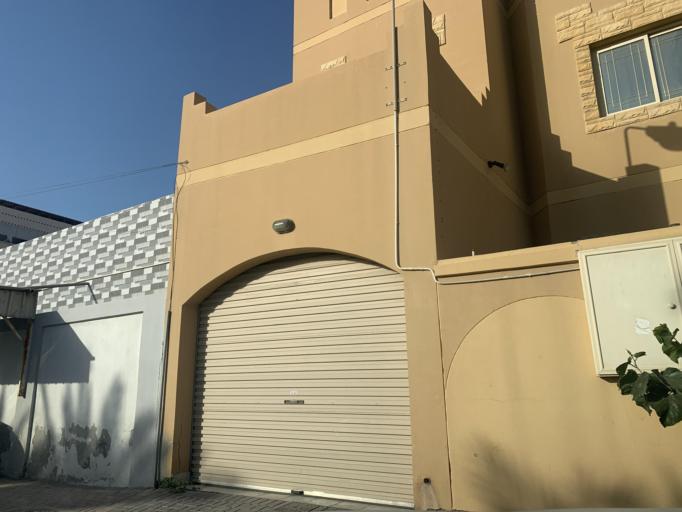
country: BH
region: Manama
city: Jidd Hafs
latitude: 26.2232
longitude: 50.5336
